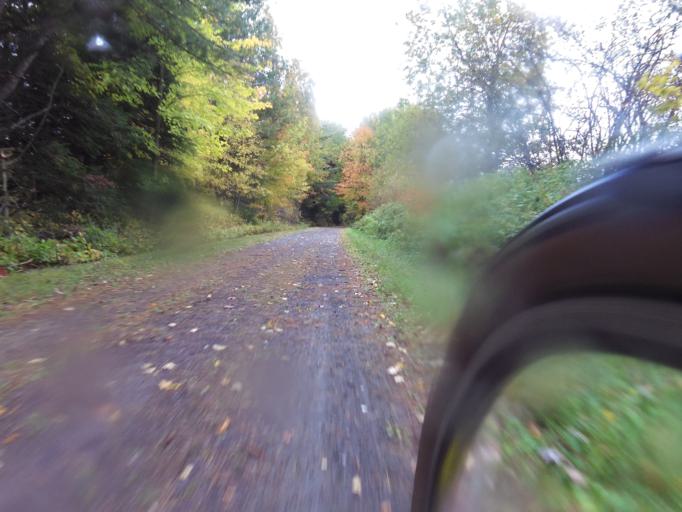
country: CA
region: Quebec
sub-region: Outaouais
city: Shawville
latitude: 45.6743
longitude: -76.5428
